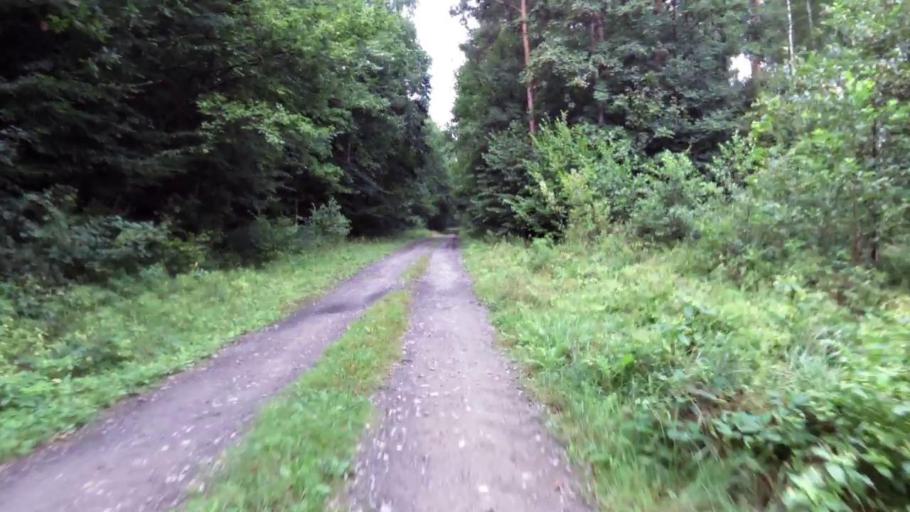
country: PL
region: West Pomeranian Voivodeship
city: Trzcinsko Zdroj
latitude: 52.8733
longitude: 14.6877
